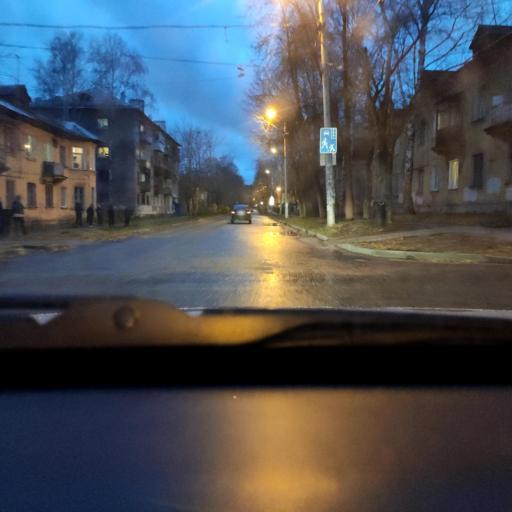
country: RU
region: Perm
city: Kondratovo
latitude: 58.0404
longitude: 56.1084
